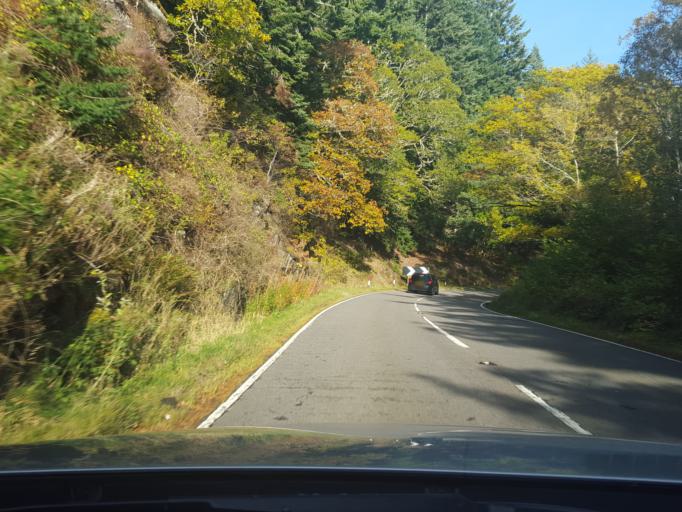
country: GB
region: Scotland
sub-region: Highland
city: Beauly
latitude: 57.2809
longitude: -4.4920
